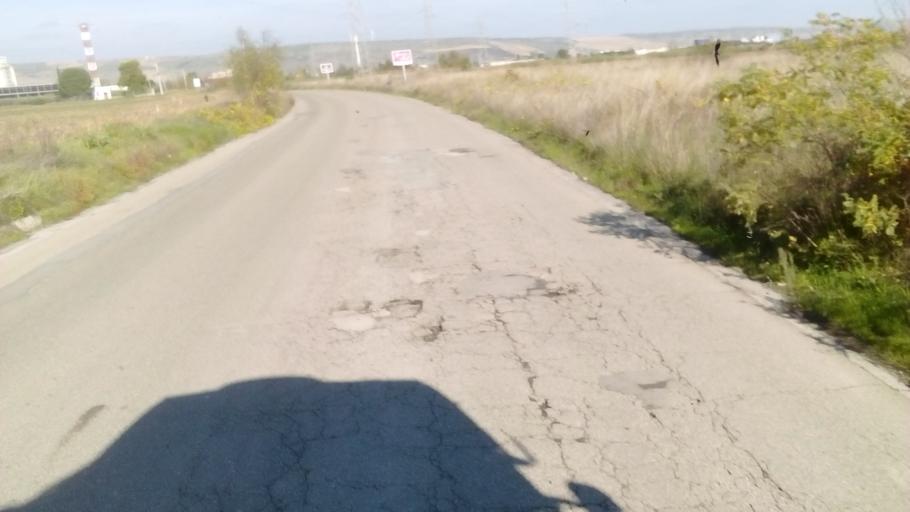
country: IT
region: Basilicate
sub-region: Provincia di Potenza
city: Melfi
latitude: 41.0668
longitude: 15.6823
